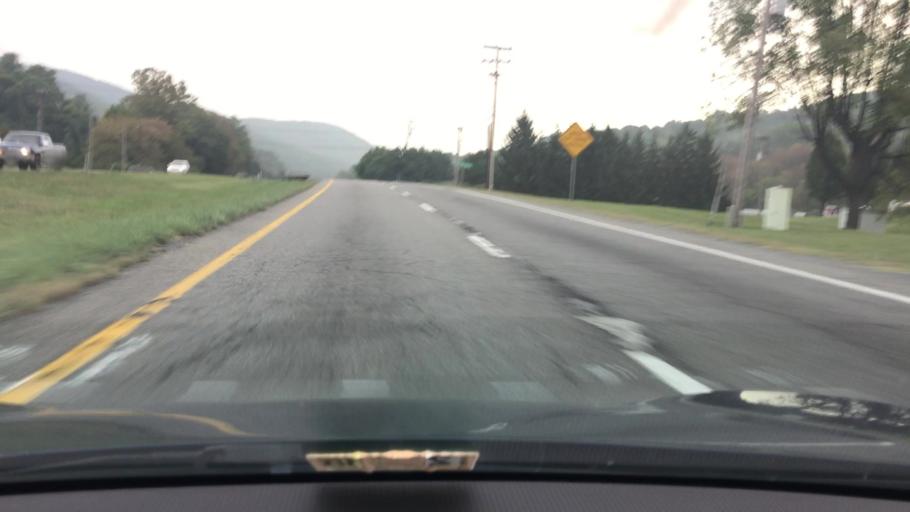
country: US
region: Virginia
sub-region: Botetourt County
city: Blue Ridge
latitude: 37.3852
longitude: -79.7975
